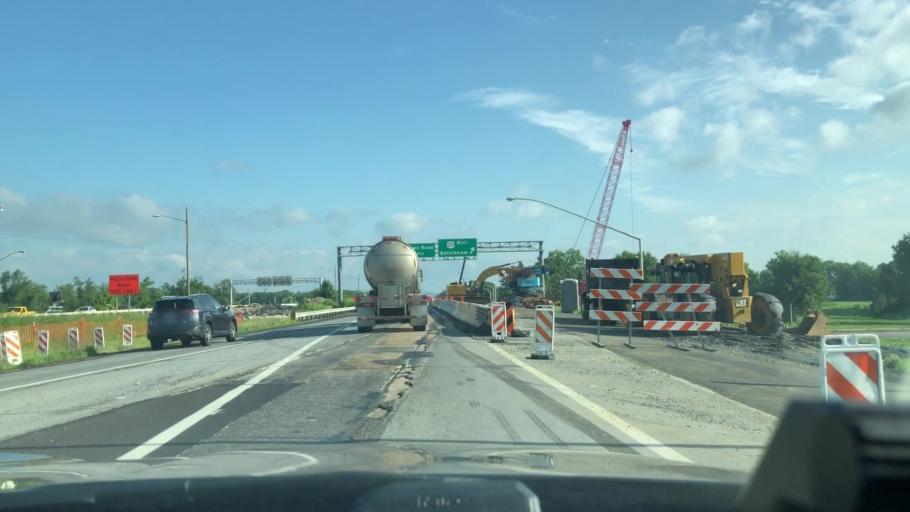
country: US
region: Pennsylvania
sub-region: Northampton County
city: Palmer Heights
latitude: 40.6818
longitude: -75.2884
